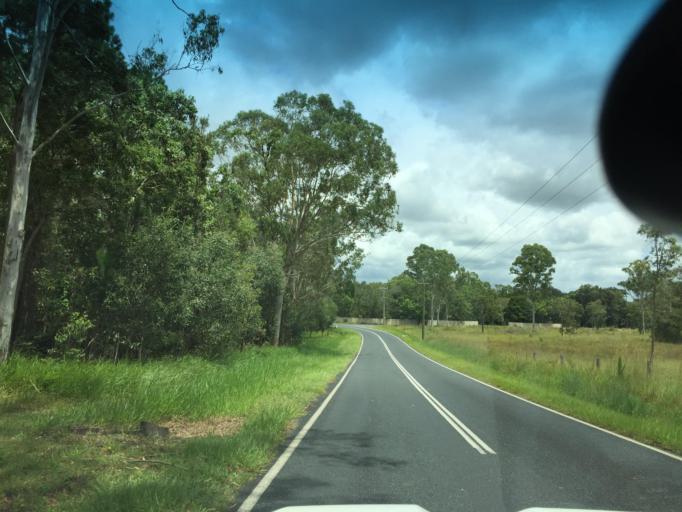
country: AU
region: Queensland
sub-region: Moreton Bay
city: Caboolture
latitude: -27.0457
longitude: 152.9136
